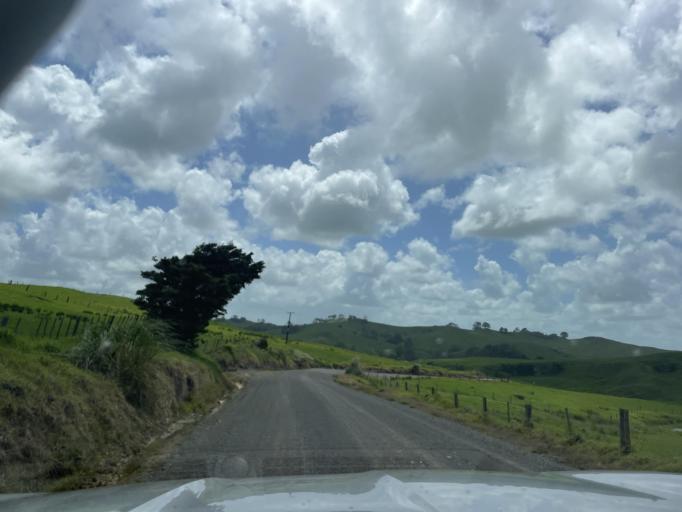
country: NZ
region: Auckland
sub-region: Auckland
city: Wellsford
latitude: -36.1973
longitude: 174.3364
